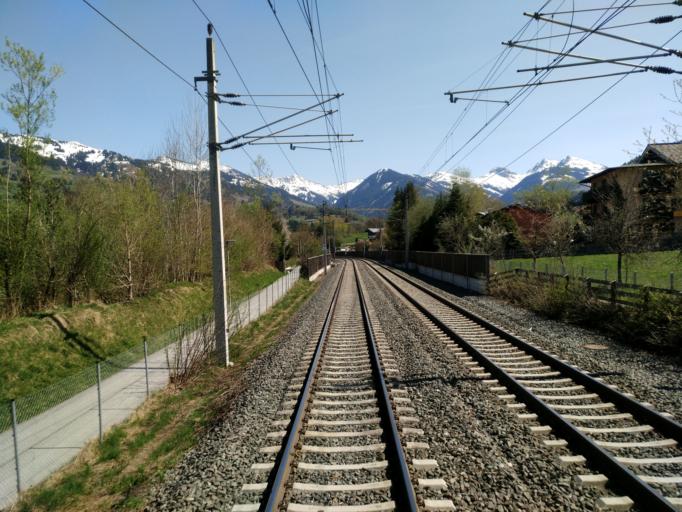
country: AT
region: Tyrol
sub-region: Politischer Bezirk Kitzbuhel
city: Kitzbuhel
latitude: 47.4422
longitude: 12.3922
